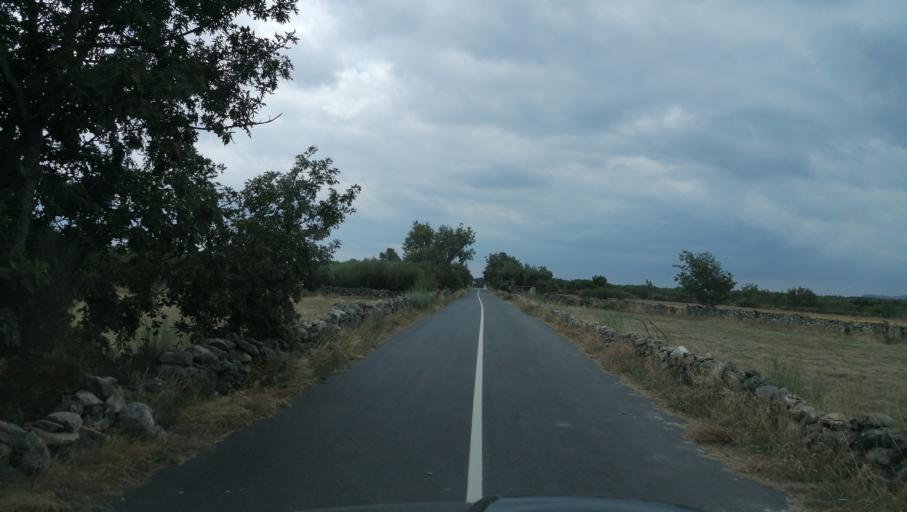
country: PT
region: Vila Real
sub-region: Vila Pouca de Aguiar
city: Vila Pouca de Aguiar
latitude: 41.5476
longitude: -7.6629
